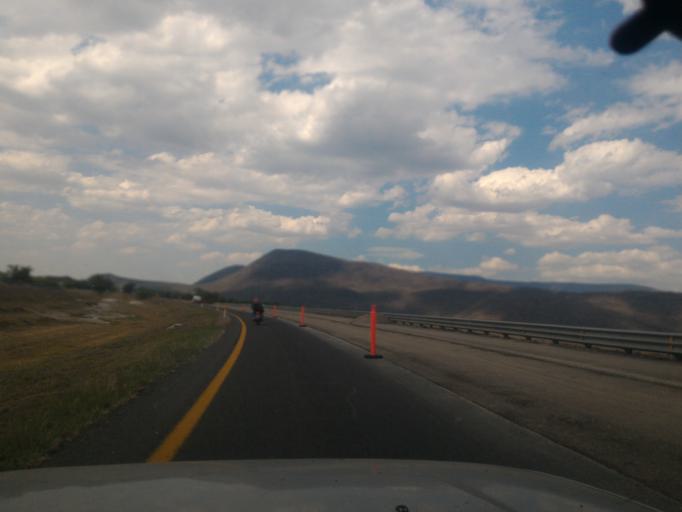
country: MX
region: Jalisco
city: Zacoalco de Torres
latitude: 20.1612
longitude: -103.5010
